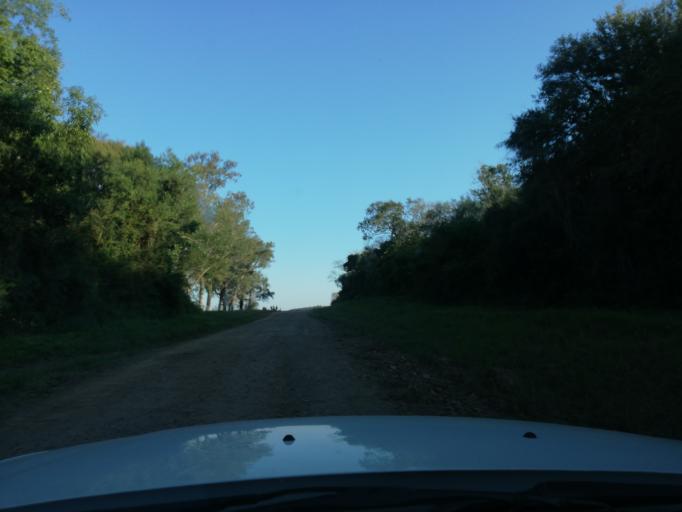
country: AR
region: Misiones
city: Cerro Cora
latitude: -27.6247
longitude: -55.7039
